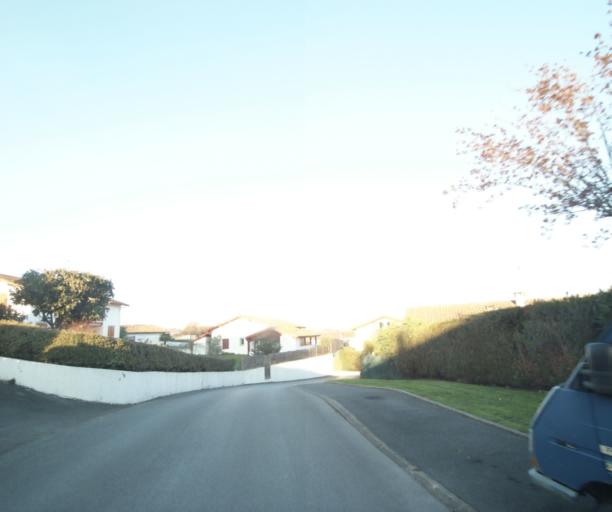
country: FR
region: Aquitaine
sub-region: Departement des Pyrenees-Atlantiques
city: Urrugne
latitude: 43.3661
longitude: -1.6954
